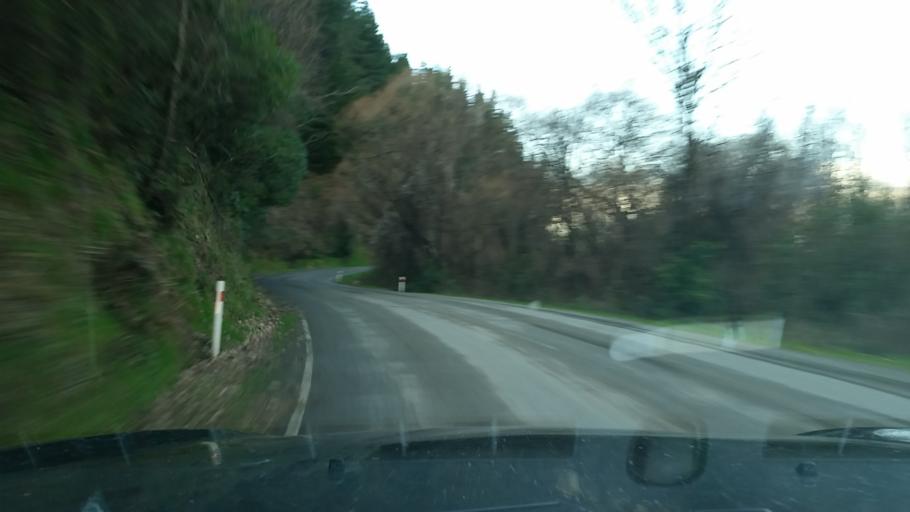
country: NZ
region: Marlborough
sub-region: Marlborough District
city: Blenheim
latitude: -41.5196
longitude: 173.6028
